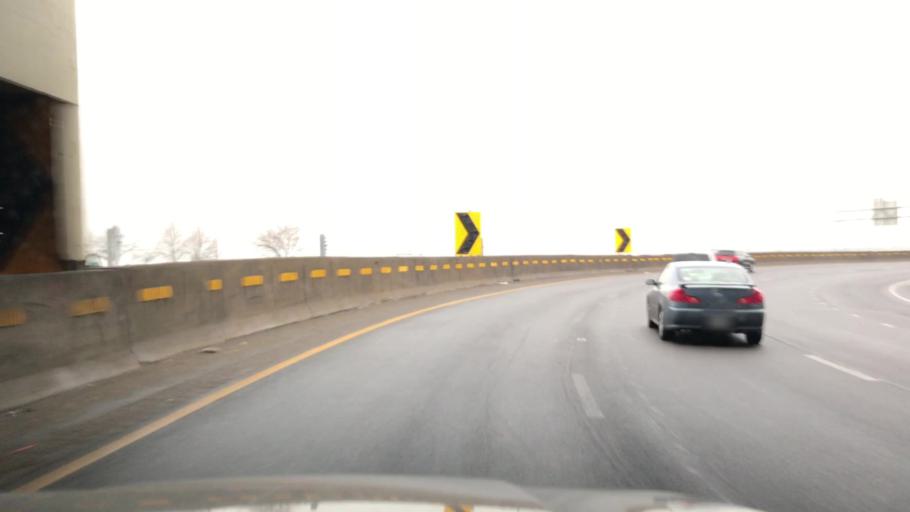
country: US
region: Ohio
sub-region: Cuyahoga County
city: Cleveland
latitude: 41.5170
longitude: -81.6754
